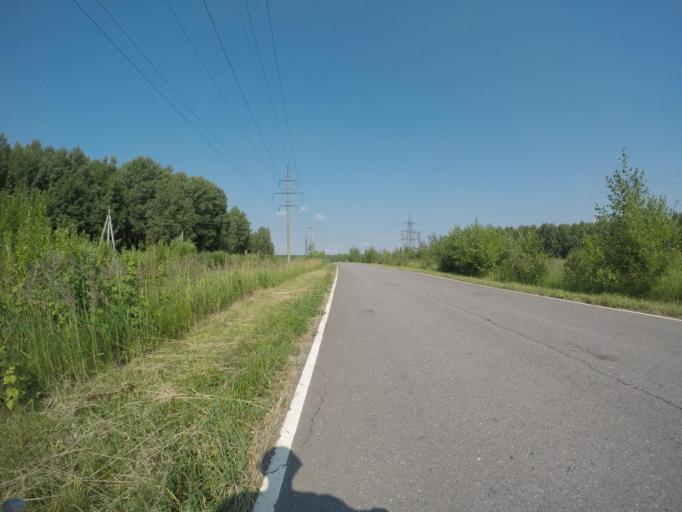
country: RU
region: Moskovskaya
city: Rechitsy
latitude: 55.6263
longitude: 38.5196
